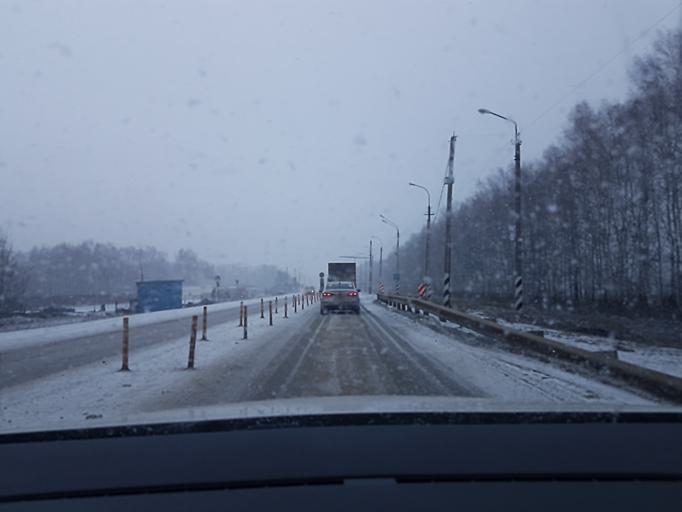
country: RU
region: Tambov
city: Pervomayskiy
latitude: 53.3106
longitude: 40.2203
